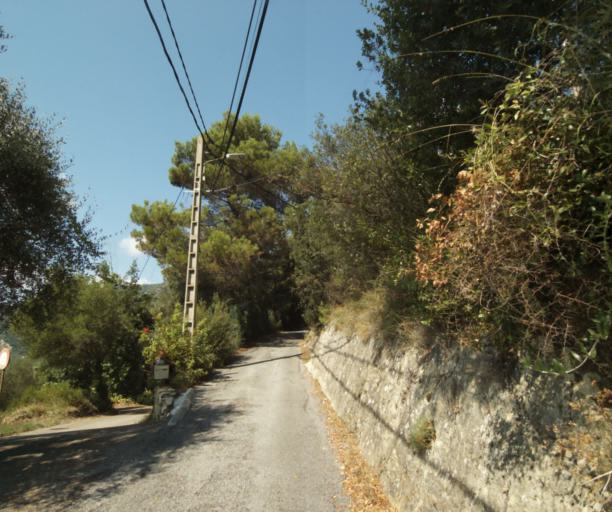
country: FR
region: Provence-Alpes-Cote d'Azur
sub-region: Departement des Alpes-Maritimes
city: Drap
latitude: 43.7609
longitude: 7.3260
